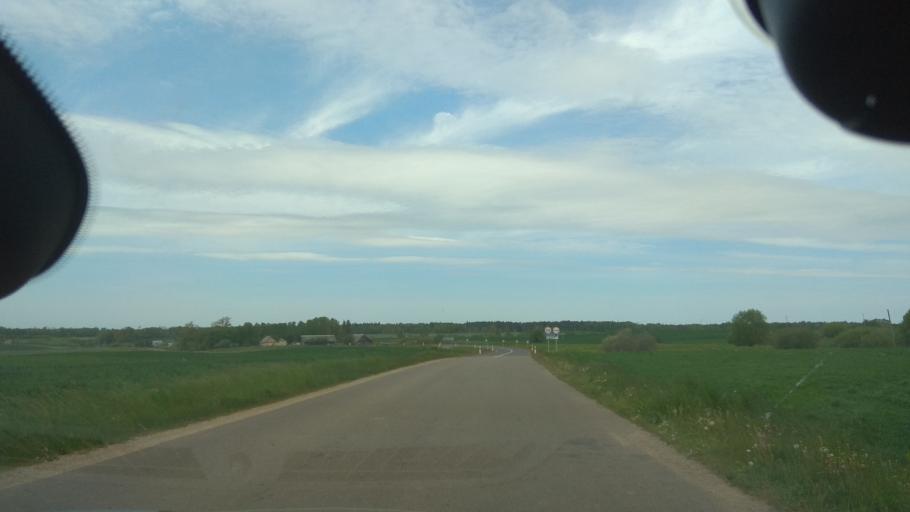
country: LT
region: Vilnius County
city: Ukmerge
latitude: 55.1046
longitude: 24.6825
